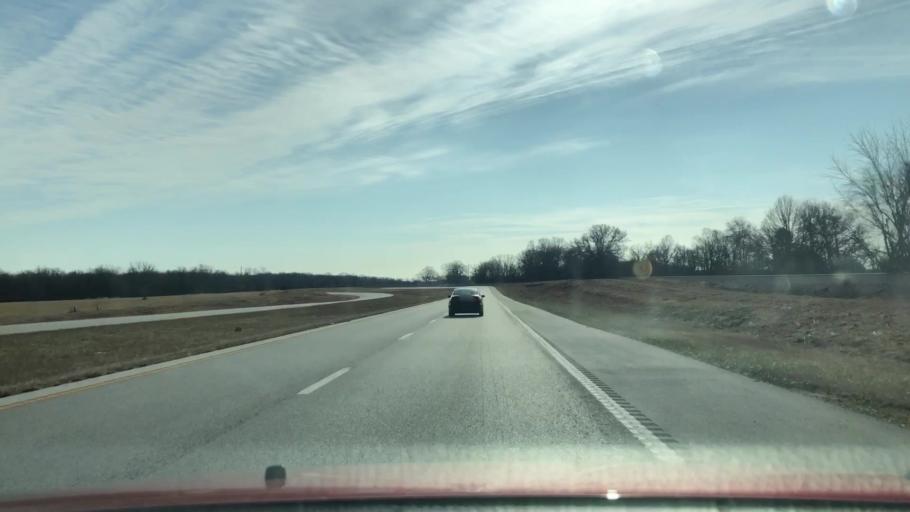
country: US
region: Missouri
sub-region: Webster County
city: Seymour
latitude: 37.1362
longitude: -92.7435
